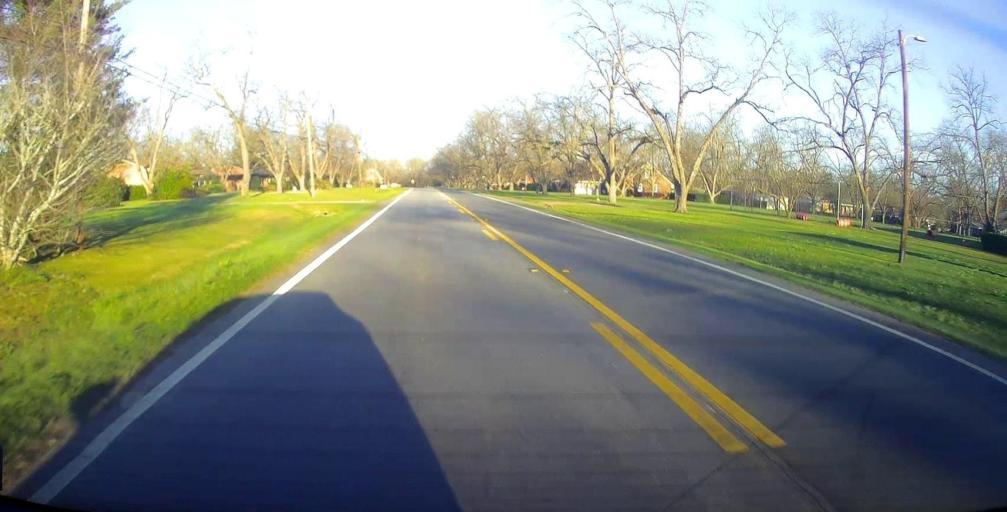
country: US
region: Georgia
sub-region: Wilcox County
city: Rochelle
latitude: 31.9508
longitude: -83.4448
